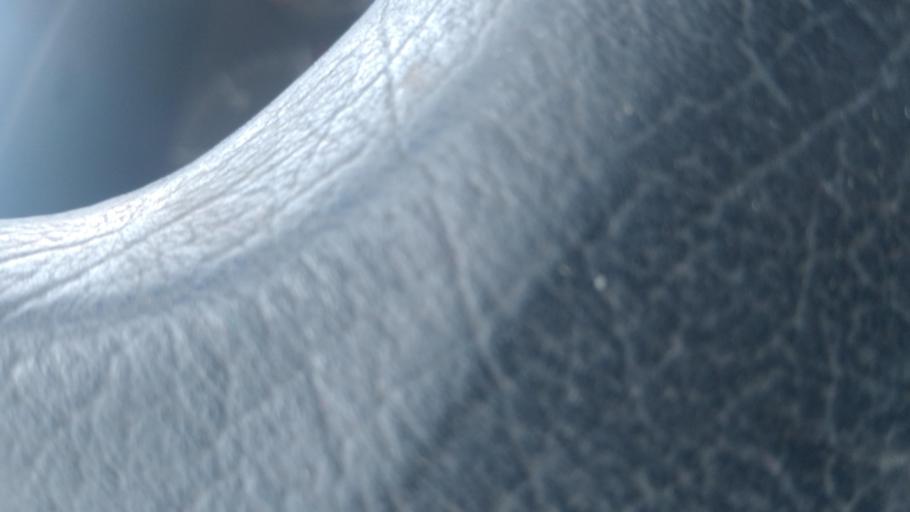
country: MR
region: Nouakchott
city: Nouakchott
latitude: 18.0579
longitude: -15.9680
